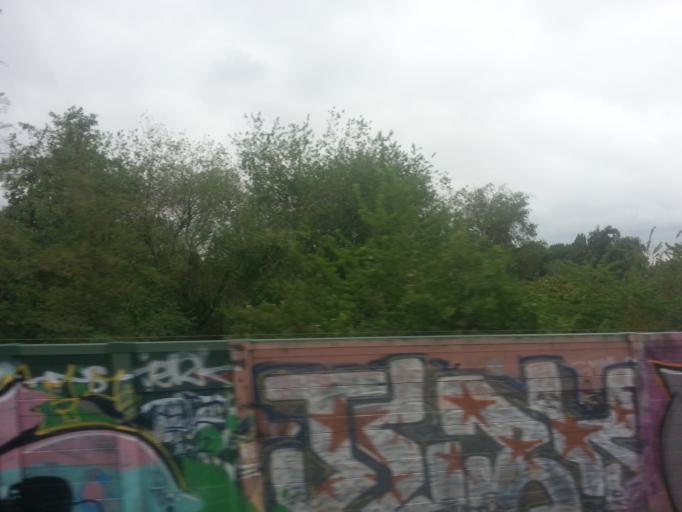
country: NL
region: South Holland
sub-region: Gemeente Spijkenisse
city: Spijkenisse
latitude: 51.8573
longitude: 4.3643
